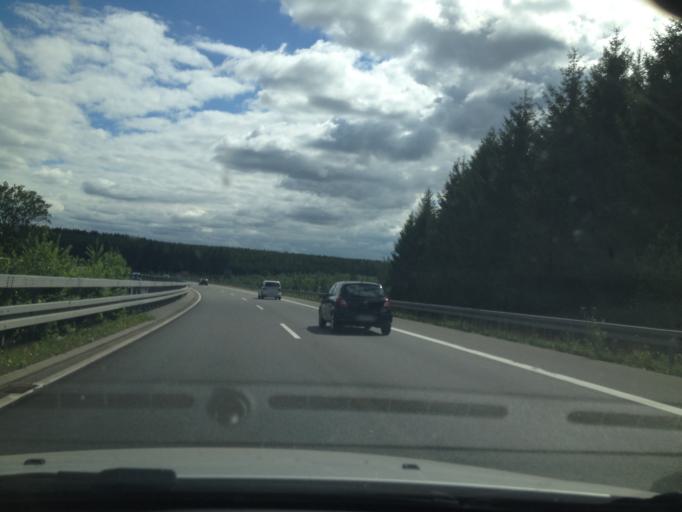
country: DE
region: North Rhine-Westphalia
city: Kreuztal
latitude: 50.9759
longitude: 7.9398
